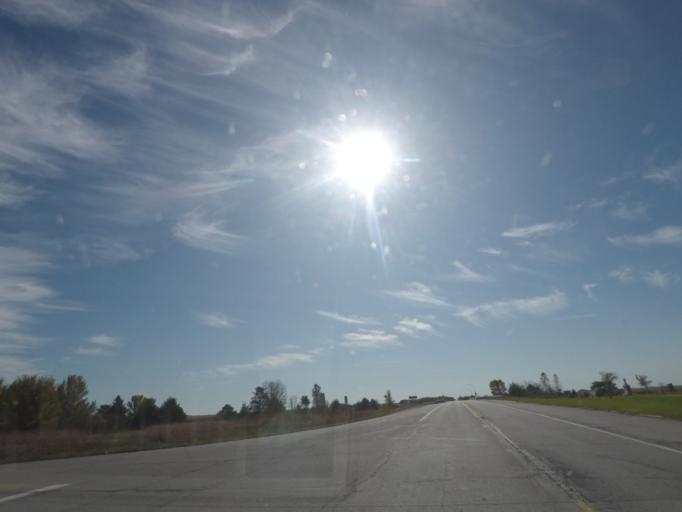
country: US
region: Iowa
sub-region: Story County
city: Nevada
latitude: 42.0092
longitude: -93.3094
